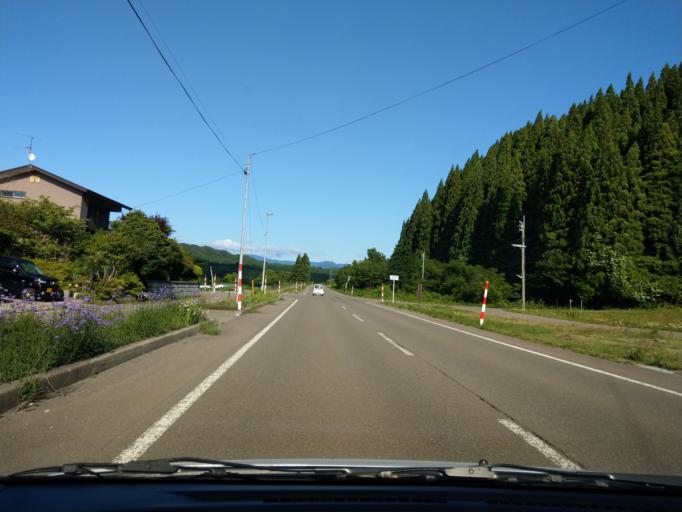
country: JP
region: Akita
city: Takanosu
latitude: 40.1185
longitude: 140.3851
